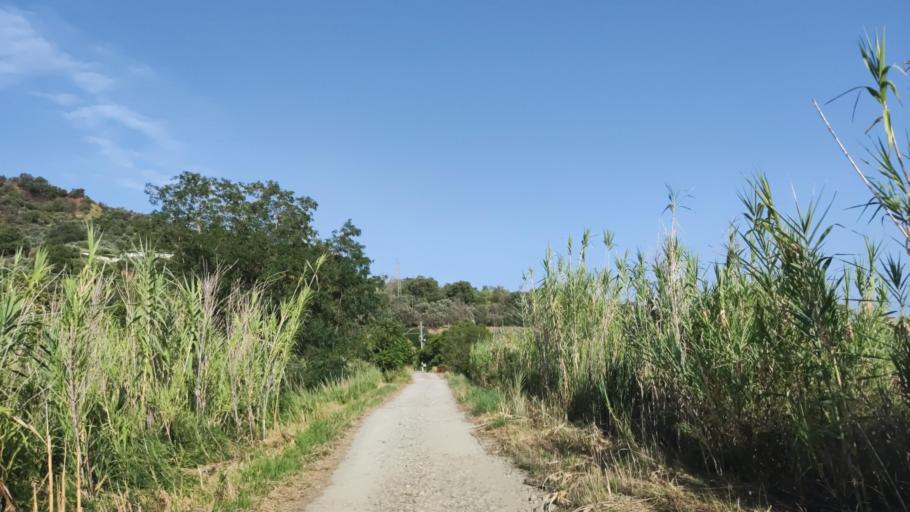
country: IT
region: Calabria
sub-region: Provincia di Reggio Calabria
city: Grotteria
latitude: 38.3494
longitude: 16.2584
